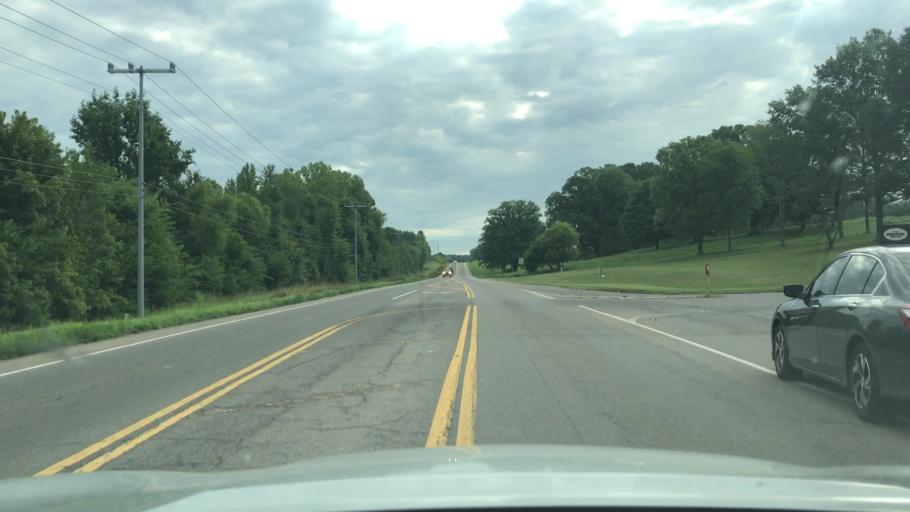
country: US
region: Kentucky
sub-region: Todd County
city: Guthrie
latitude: 36.6224
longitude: -87.2296
